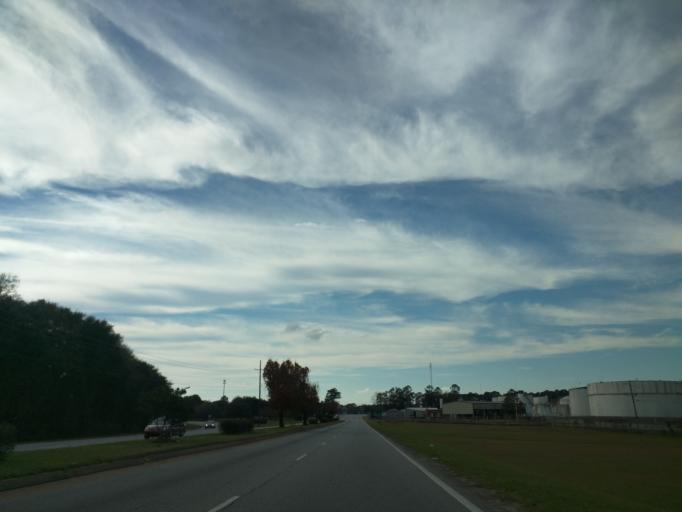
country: US
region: Georgia
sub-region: Decatur County
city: Bainbridge
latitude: 30.9032
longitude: -84.5390
